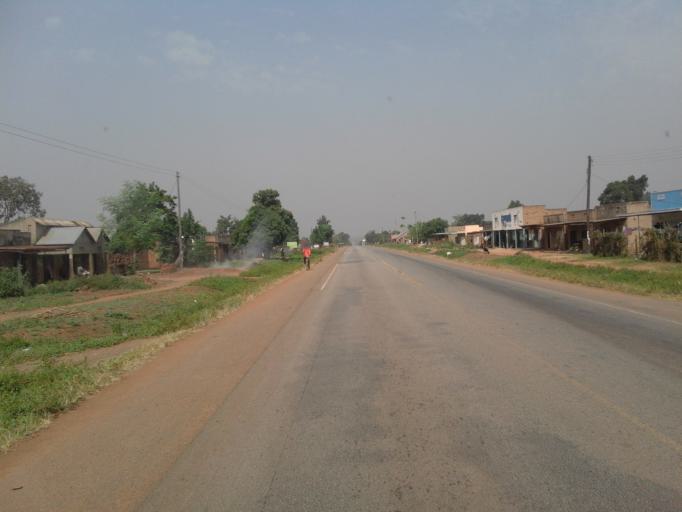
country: UG
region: Eastern Region
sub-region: Bugiri District
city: Bugiri
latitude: 0.6043
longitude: 33.6906
